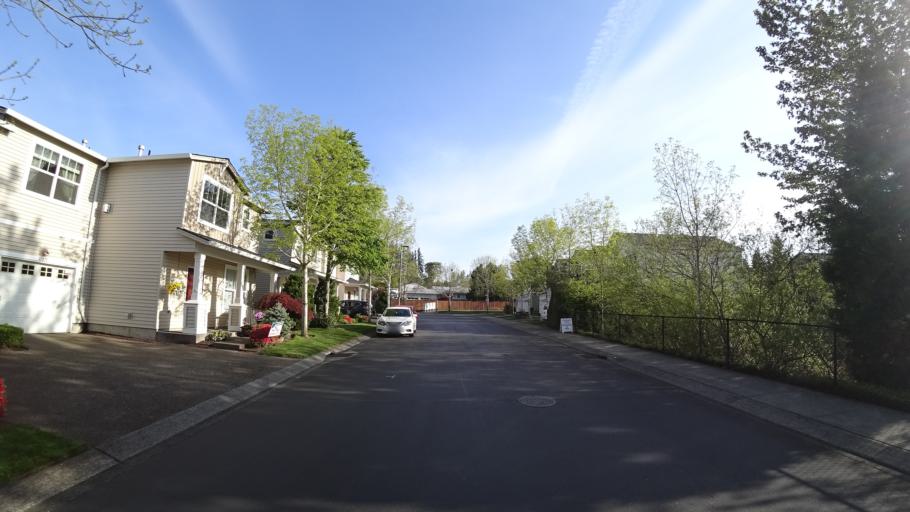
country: US
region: Oregon
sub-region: Washington County
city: King City
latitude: 45.4272
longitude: -122.8424
